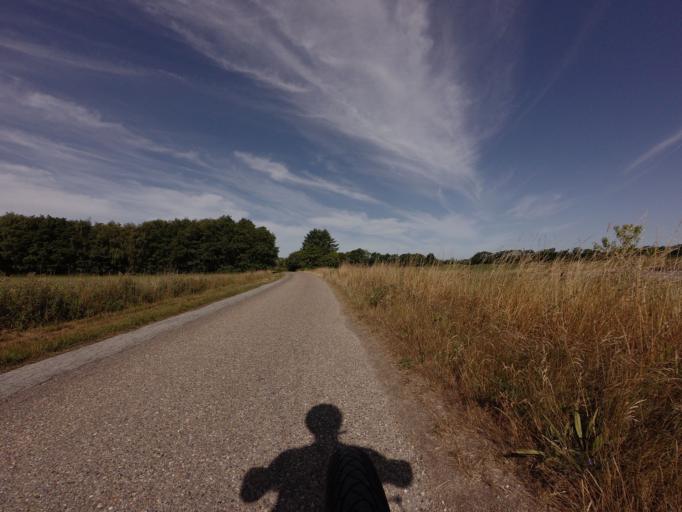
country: DK
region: North Denmark
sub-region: Hjorring Kommune
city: Vra
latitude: 57.4004
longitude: 9.9485
